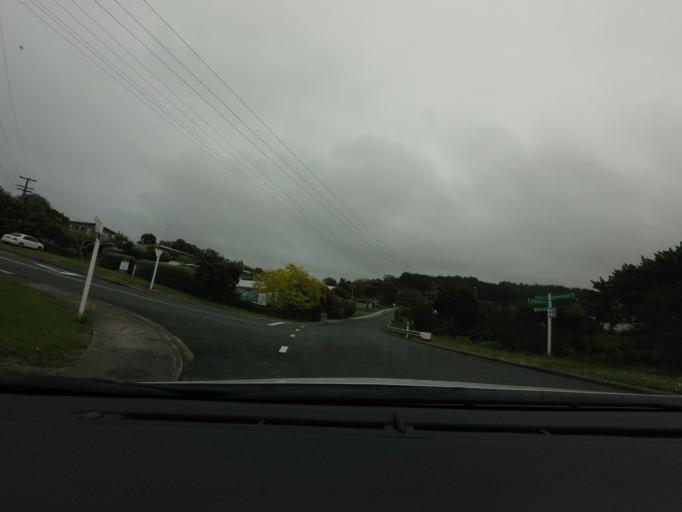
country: NZ
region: Auckland
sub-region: Auckland
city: Warkworth
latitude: -36.2901
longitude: 174.8023
